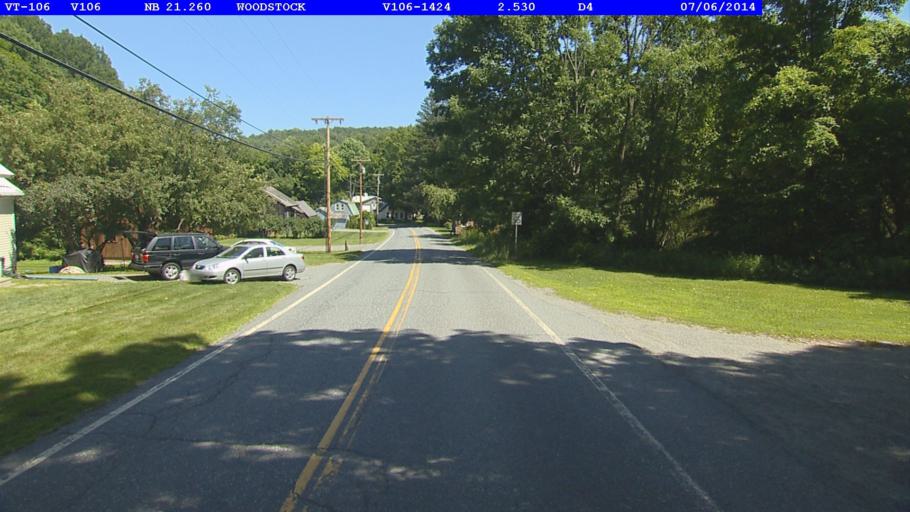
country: US
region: Vermont
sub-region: Windsor County
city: Woodstock
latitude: 43.5650
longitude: -72.5313
